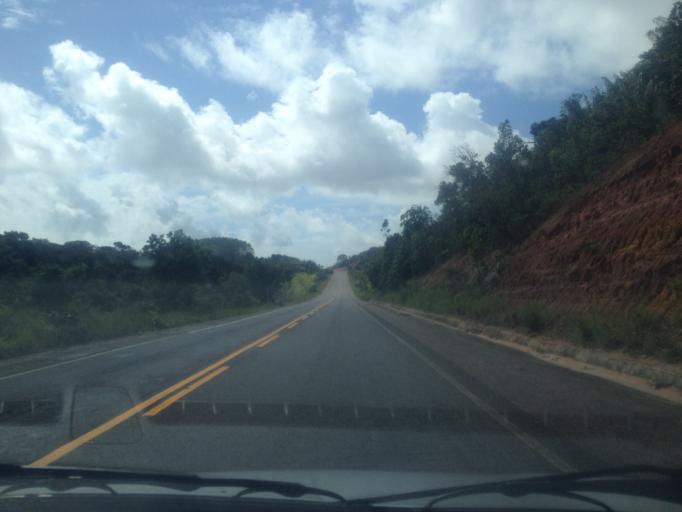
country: BR
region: Bahia
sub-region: Conde
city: Conde
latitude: -12.0264
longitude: -37.6961
